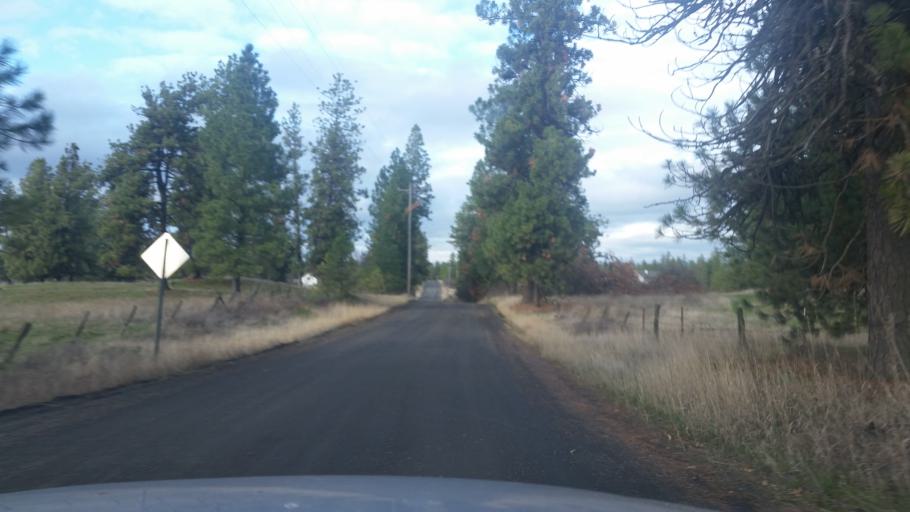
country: US
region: Washington
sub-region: Spokane County
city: Cheney
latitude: 47.4284
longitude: -117.4664
